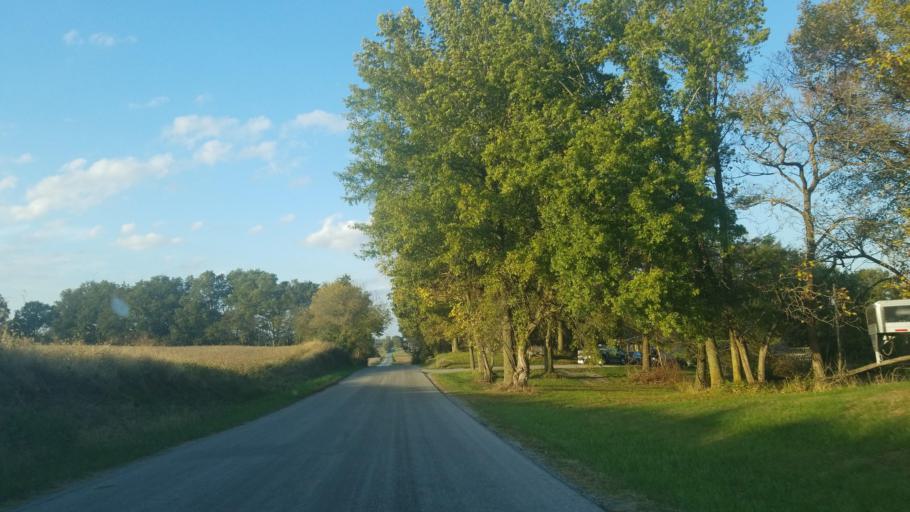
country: US
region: Illinois
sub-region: Saline County
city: Harrisburg
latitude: 37.8168
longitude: -88.6146
